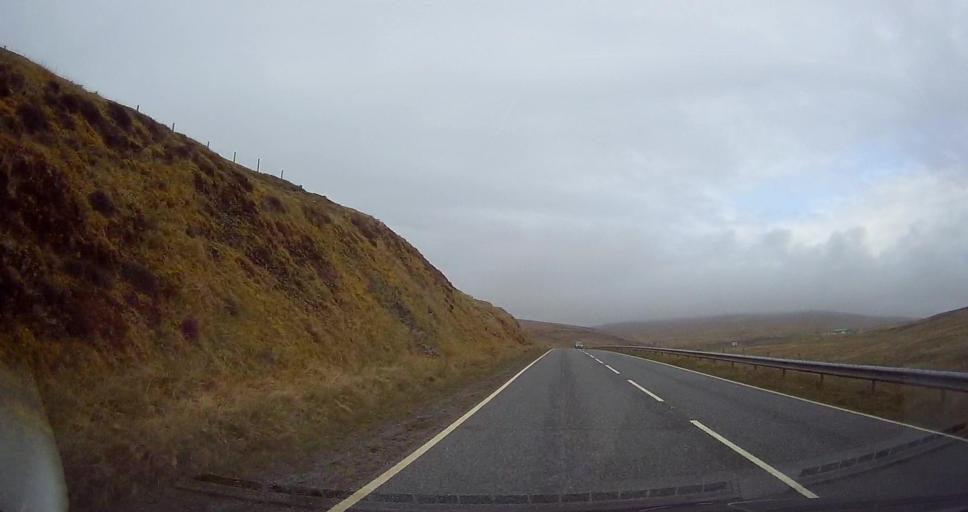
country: GB
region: Scotland
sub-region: Shetland Islands
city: Sandwick
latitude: 59.9985
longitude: -1.2794
